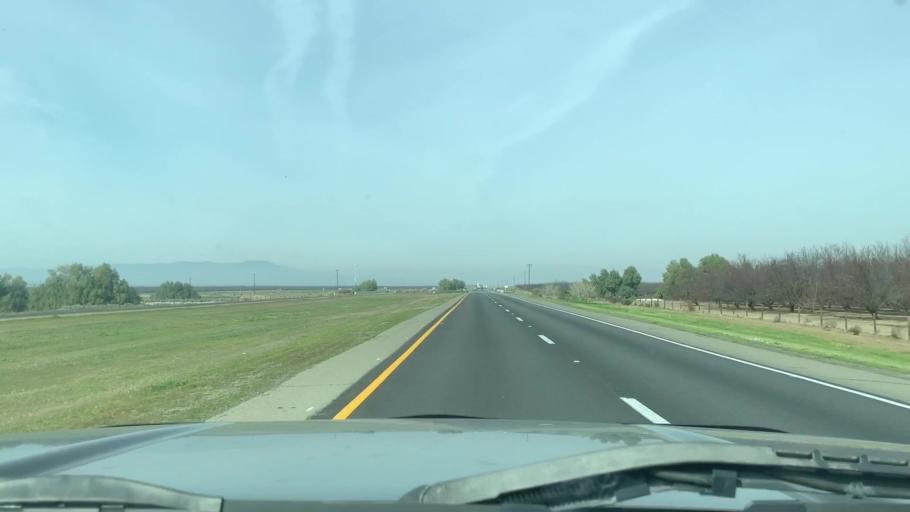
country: US
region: California
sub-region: Fresno County
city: Huron
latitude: 36.1647
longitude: -120.1833
